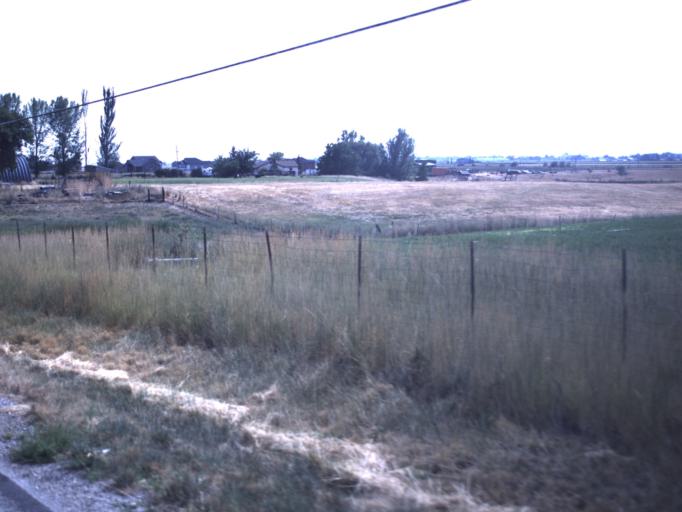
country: US
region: Utah
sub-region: Box Elder County
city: Honeyville
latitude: 41.6557
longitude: -112.0850
